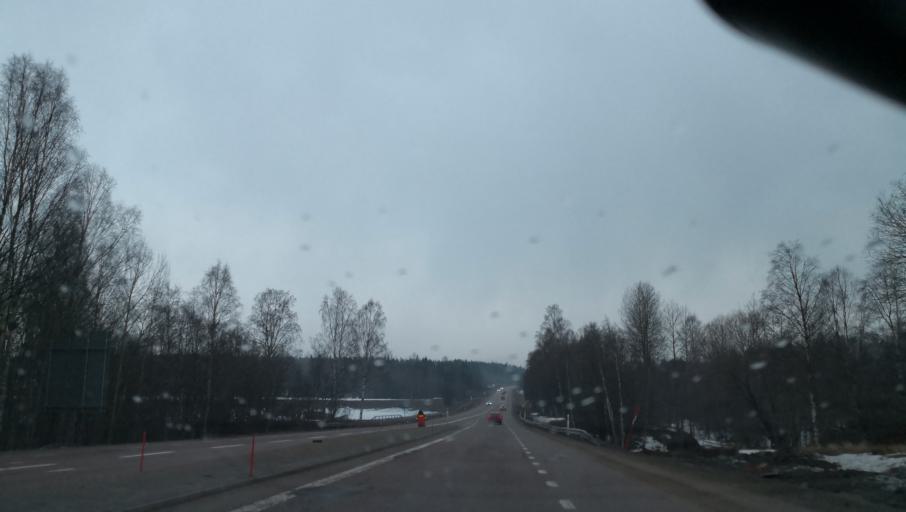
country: SE
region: Gaevleborg
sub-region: Nordanstigs Kommun
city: Bergsjoe
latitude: 62.0442
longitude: 17.2655
